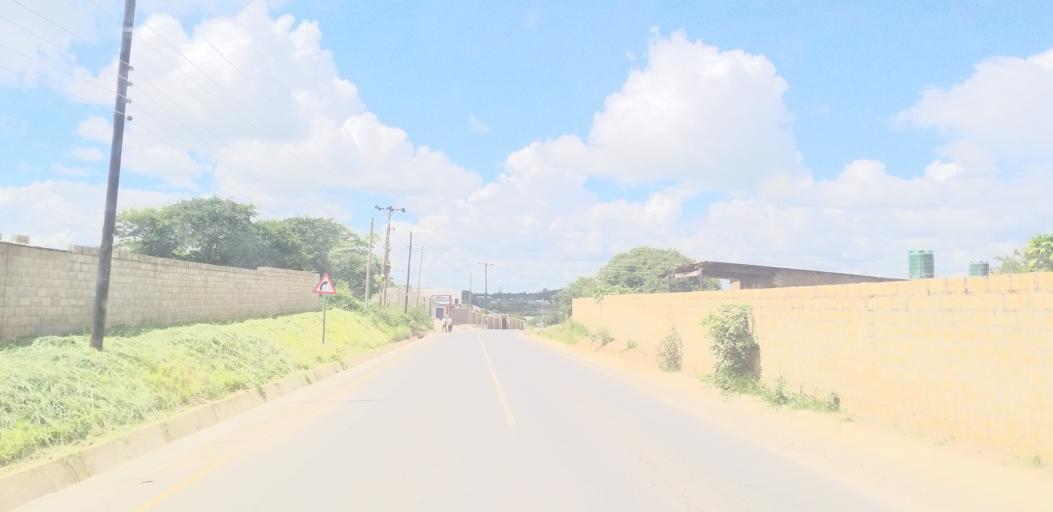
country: ZM
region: Lusaka
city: Lusaka
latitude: -15.3418
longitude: 28.3283
